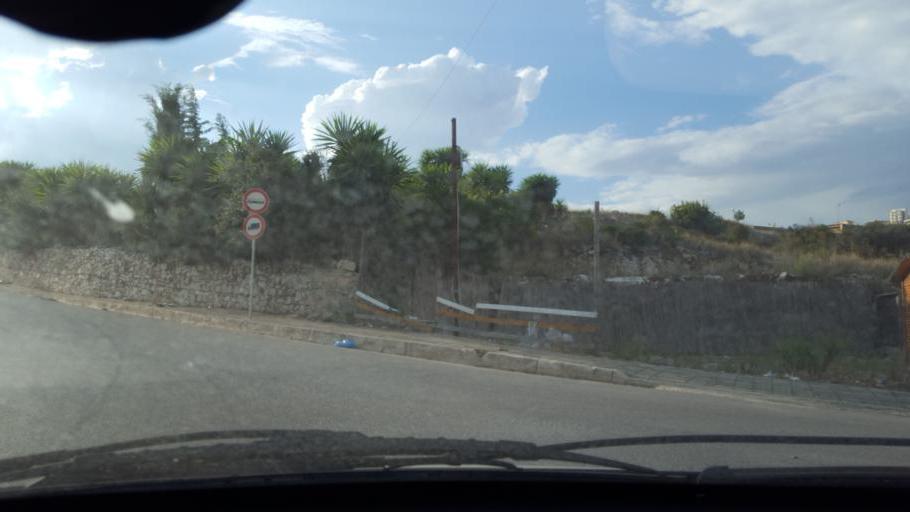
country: AL
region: Vlore
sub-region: Rrethi i Sarandes
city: Sarande
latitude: 39.8476
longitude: 20.0257
